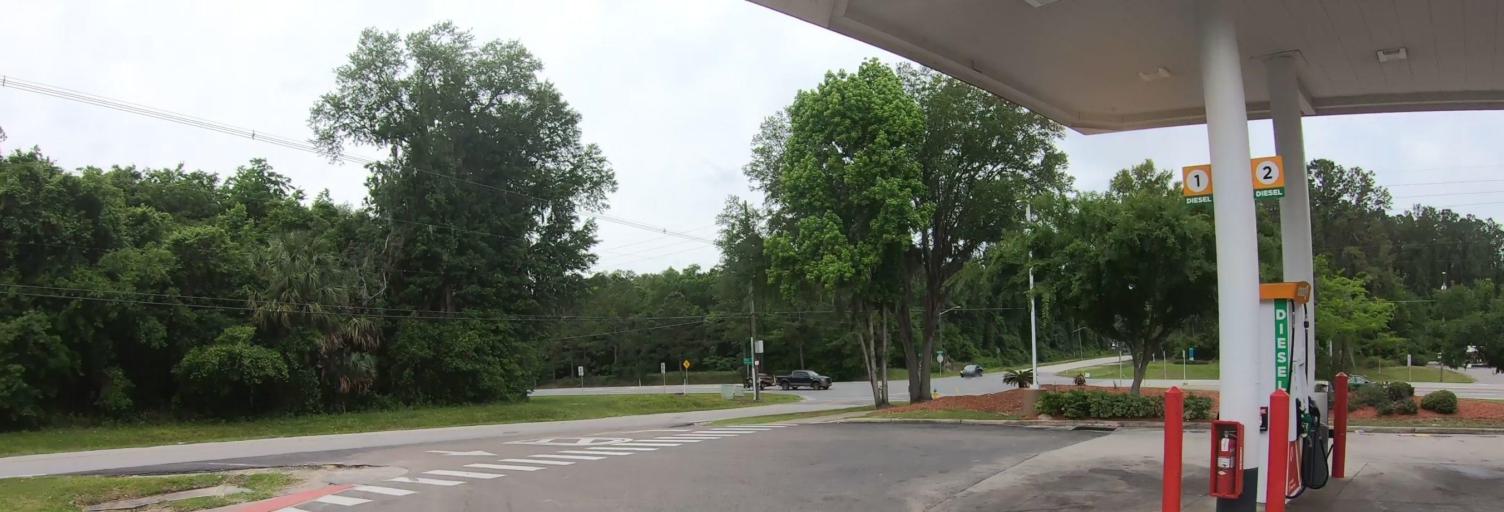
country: US
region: Florida
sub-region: Alachua County
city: Gainesville
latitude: 29.5999
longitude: -82.3747
